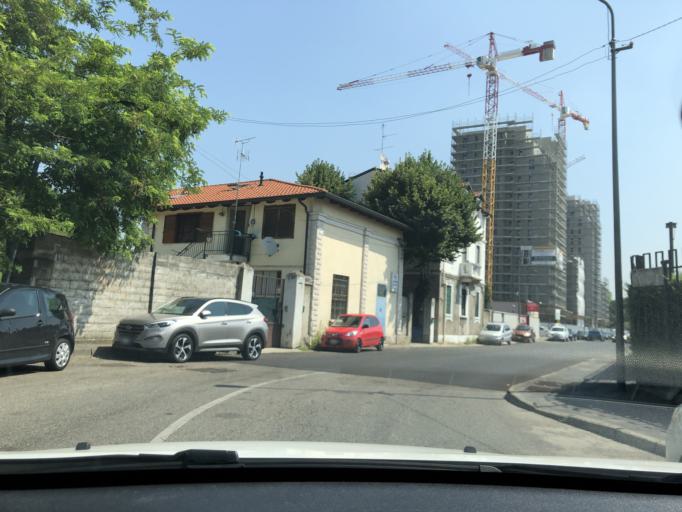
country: IT
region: Lombardy
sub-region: Citta metropolitana di Milano
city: Novate Milanese
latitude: 45.5133
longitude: 9.1615
